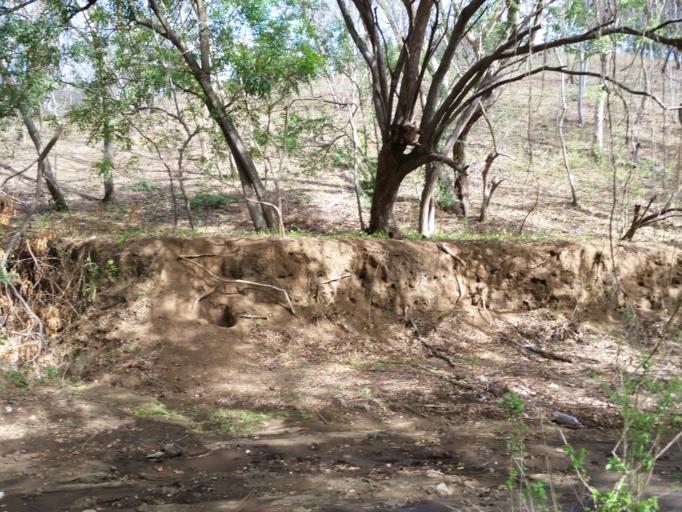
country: NI
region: Managua
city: Managua
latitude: 12.0864
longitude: -86.2505
